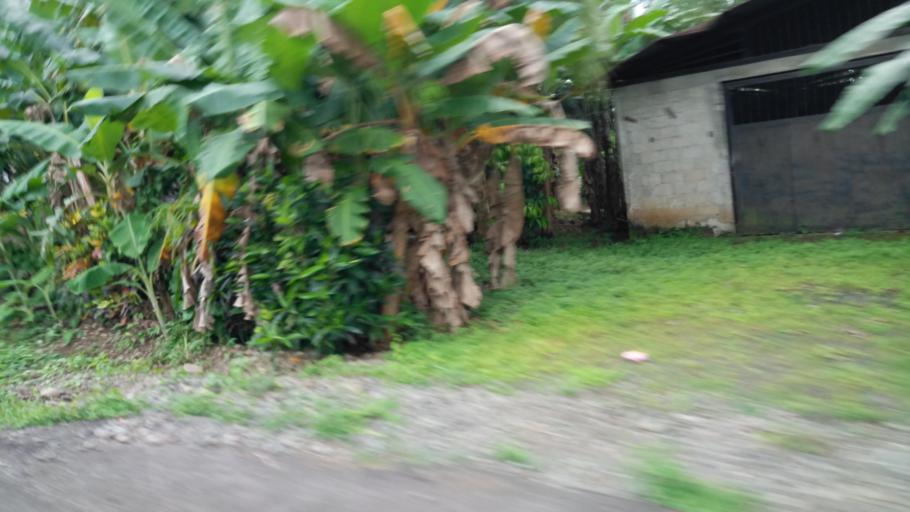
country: CR
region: Alajuela
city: Pocosol
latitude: 10.3754
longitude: -84.5530
